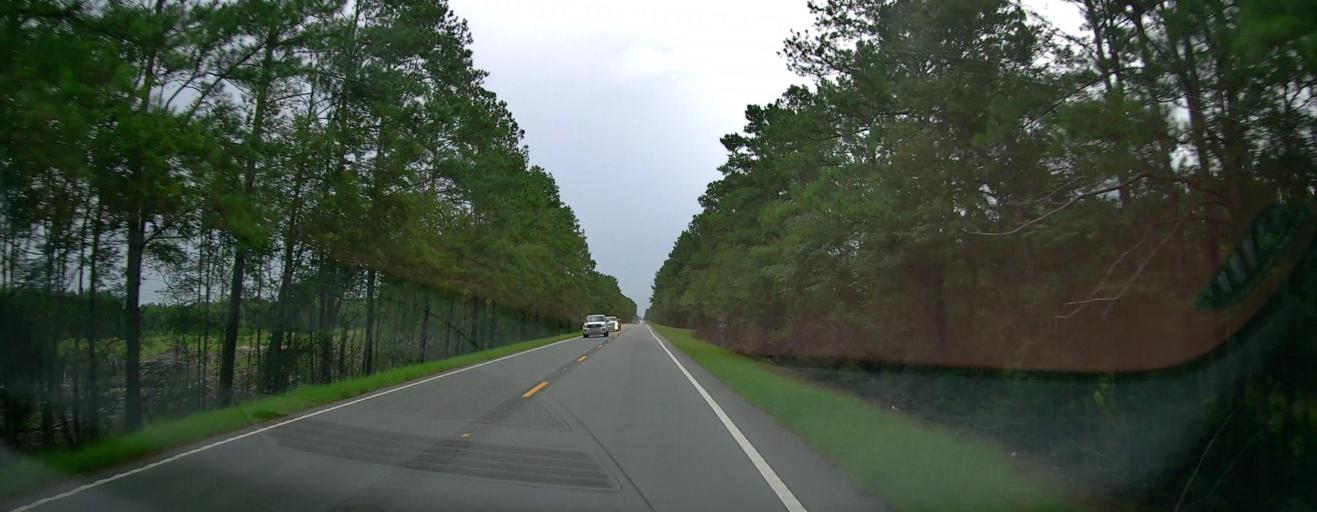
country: US
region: Georgia
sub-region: Brantley County
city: Nahunta
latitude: 31.3483
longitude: -82.0203
